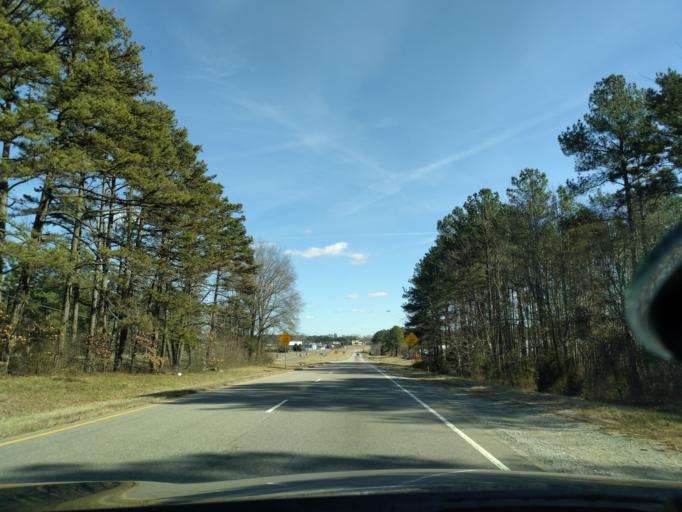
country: US
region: Virginia
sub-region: Nottoway County
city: Crewe
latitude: 37.1901
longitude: -78.1590
